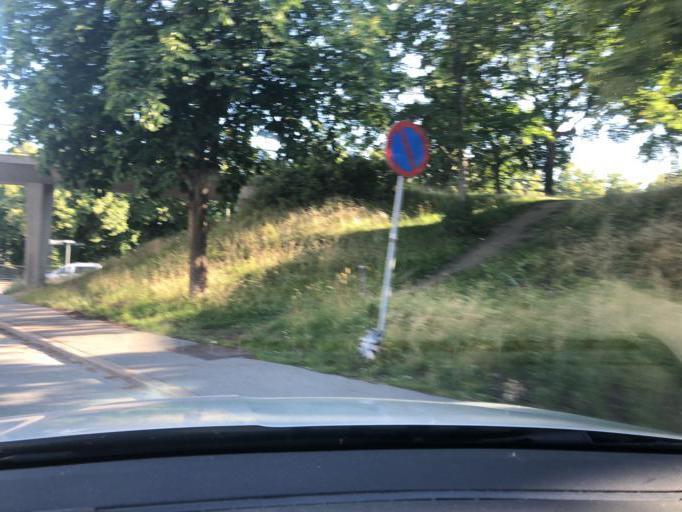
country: SE
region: Stockholm
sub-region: Huddinge Kommun
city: Segeltorp
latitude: 59.2774
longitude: 17.9022
